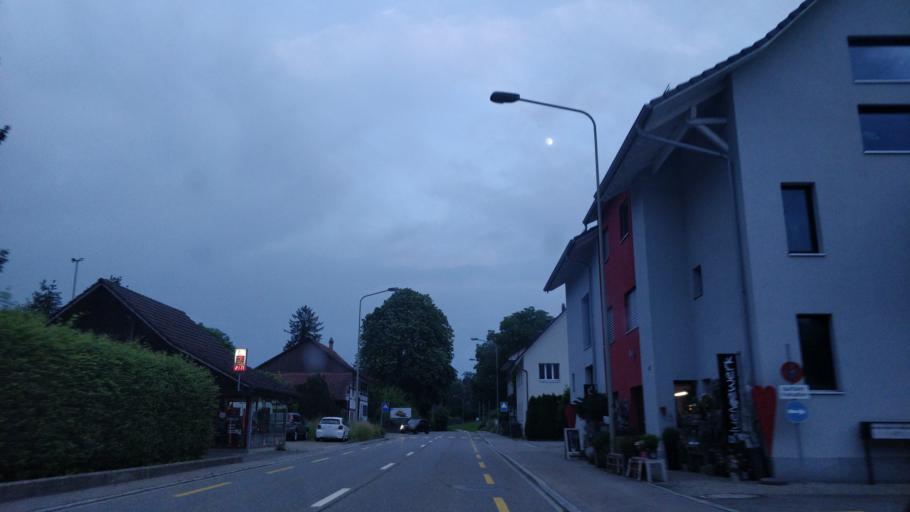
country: CH
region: Zurich
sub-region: Bezirk Buelach
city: Rorbas
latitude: 47.5296
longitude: 8.5757
